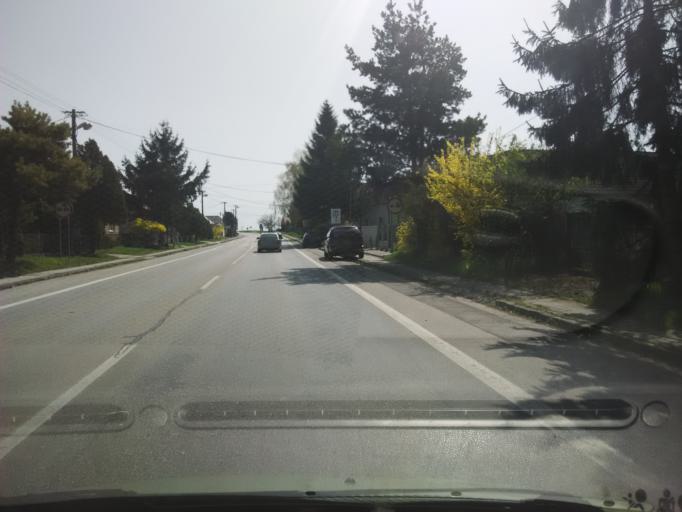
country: SK
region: Nitriansky
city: Sellye
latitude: 48.1257
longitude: 18.0297
